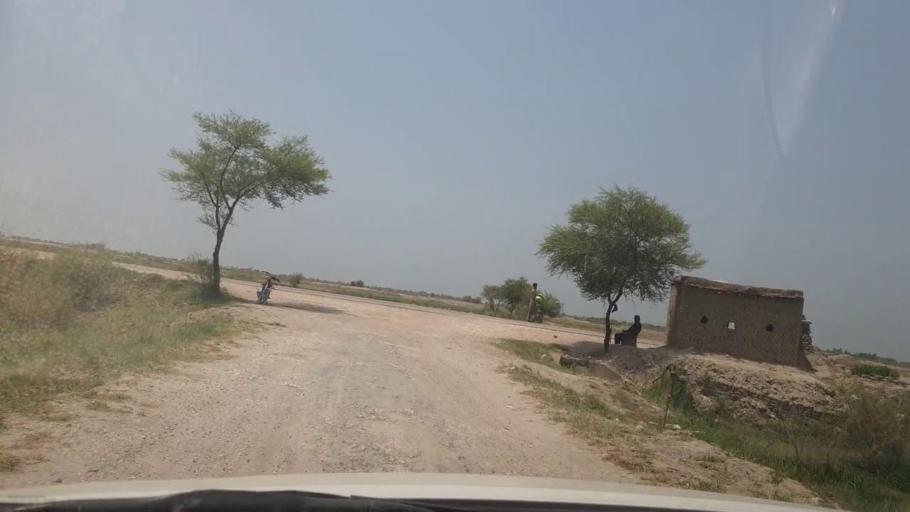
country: PK
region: Sindh
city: Rustam jo Goth
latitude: 28.0533
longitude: 68.7744
